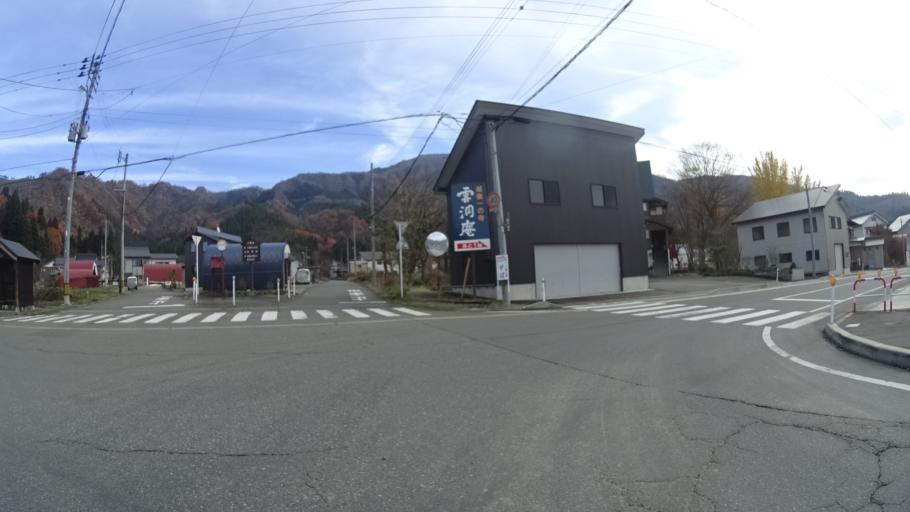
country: JP
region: Niigata
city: Muikamachi
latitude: 37.0401
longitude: 138.8923
